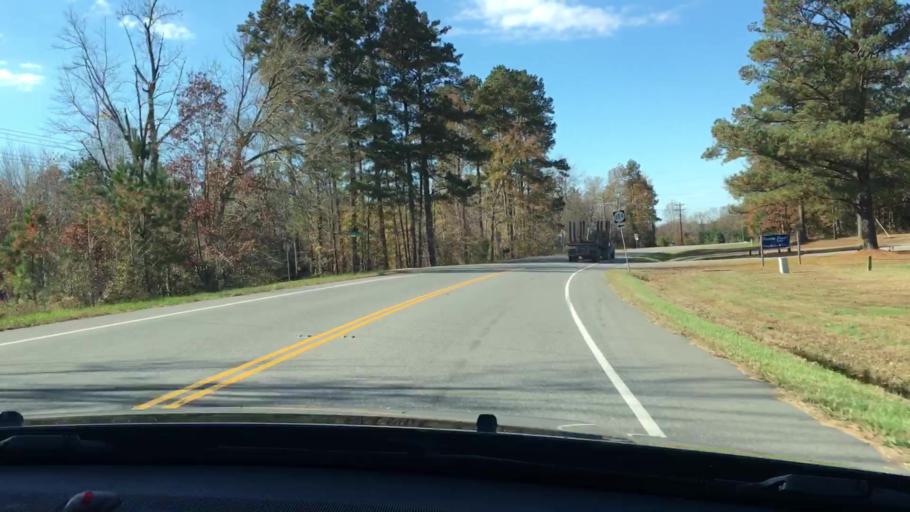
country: US
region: Virginia
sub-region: Hanover County
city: Hanover
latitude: 37.8000
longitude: -77.2598
